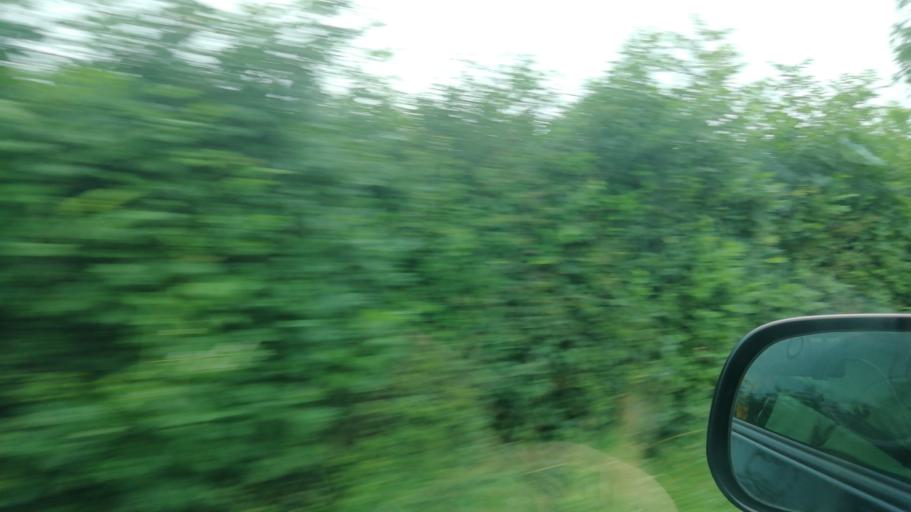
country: IE
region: Munster
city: Fethard
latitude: 52.5137
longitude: -7.6846
